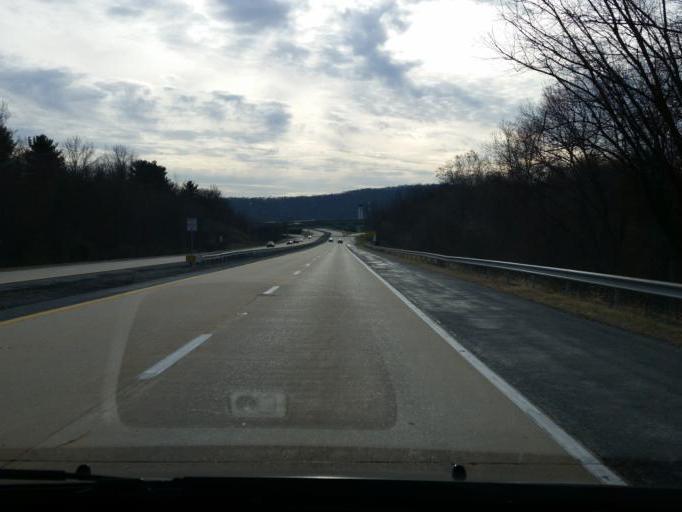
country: US
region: Pennsylvania
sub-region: Dauphin County
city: Middletown
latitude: 40.2076
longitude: -76.7548
